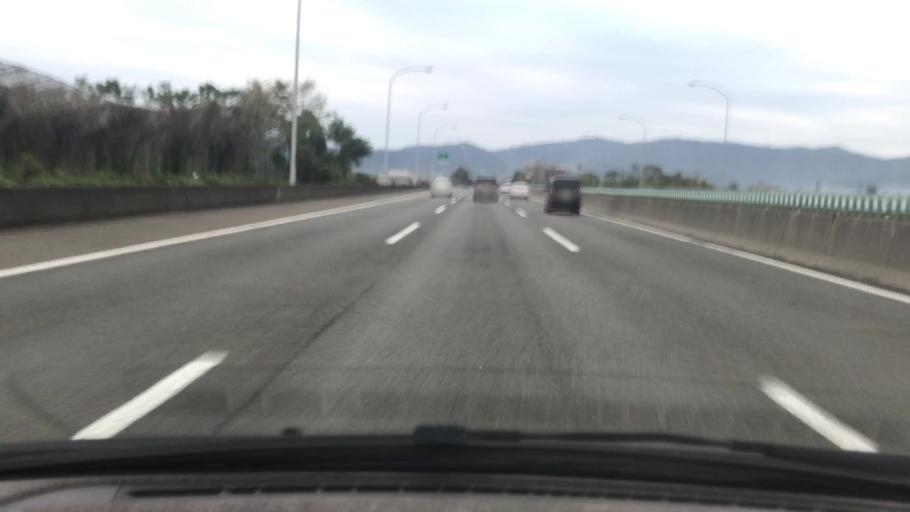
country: JP
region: Kyoto
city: Muko
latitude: 34.9508
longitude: 135.7373
